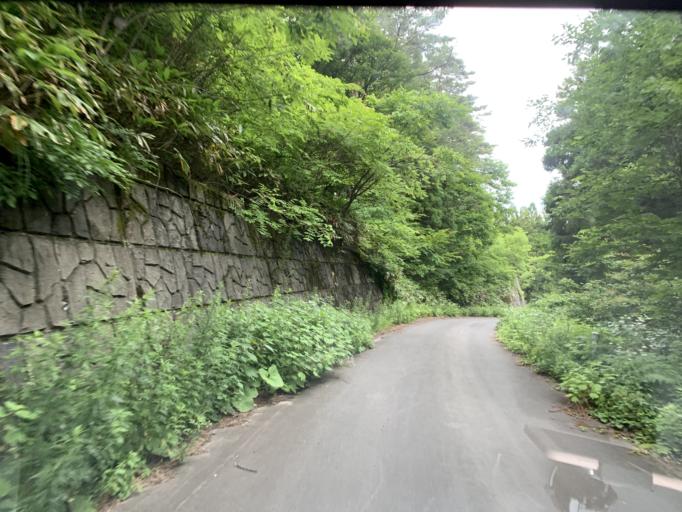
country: JP
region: Iwate
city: Ichinoseki
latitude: 38.9558
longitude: 140.8850
